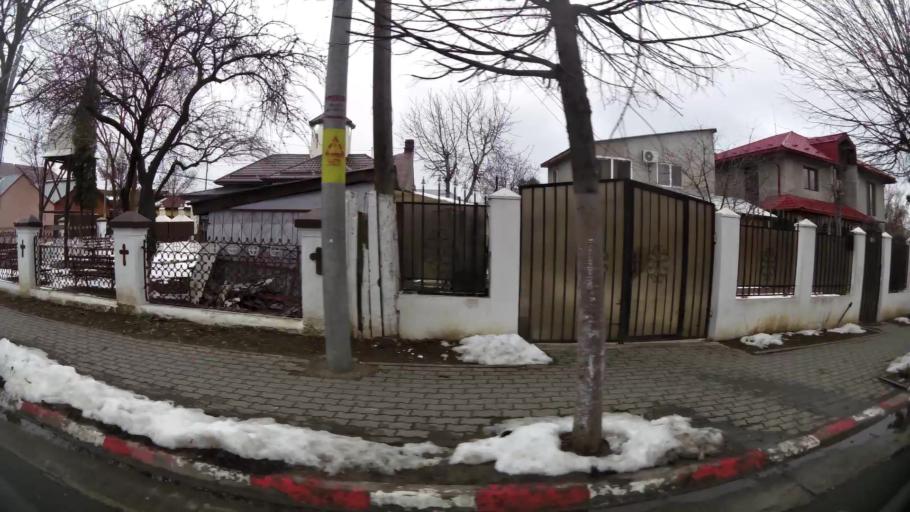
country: RO
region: Ilfov
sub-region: Voluntari City
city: Voluntari
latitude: 44.4995
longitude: 26.1974
